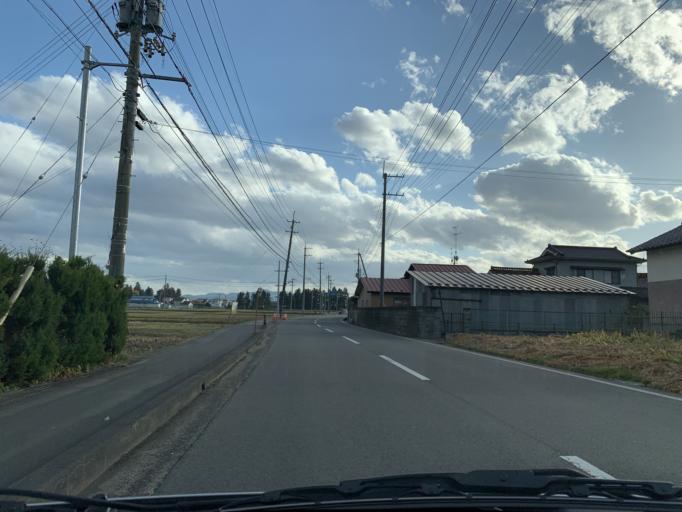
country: JP
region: Iwate
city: Mizusawa
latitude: 39.1451
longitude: 141.1589
